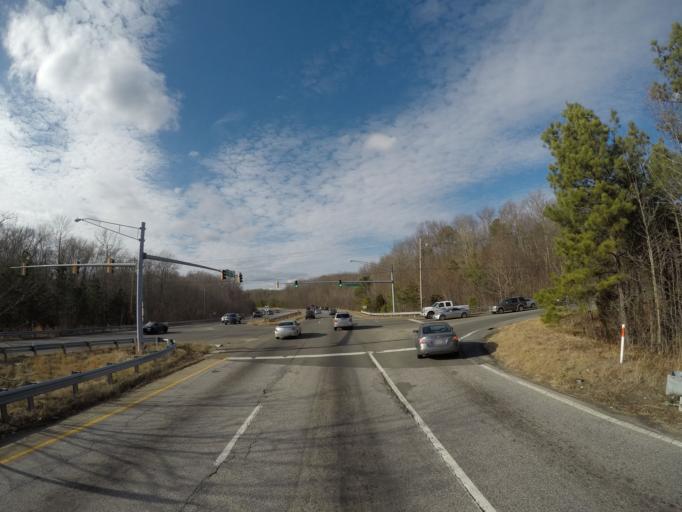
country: US
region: Maryland
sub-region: Prince George's County
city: Accokeek
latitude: 38.6551
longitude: -76.9988
